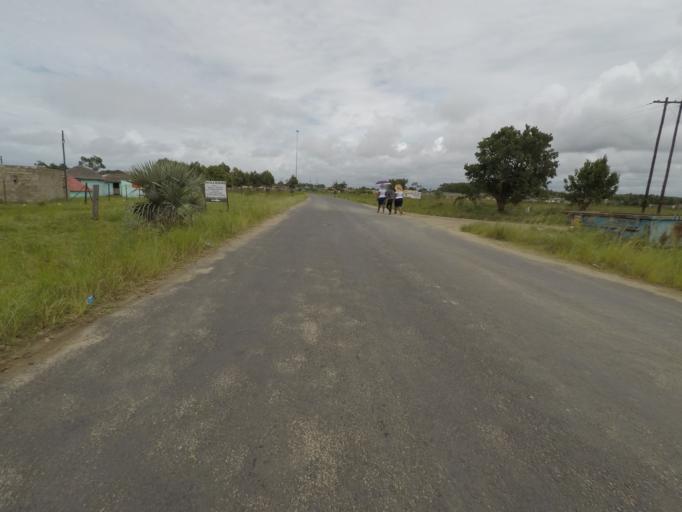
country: ZA
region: KwaZulu-Natal
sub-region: uThungulu District Municipality
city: eSikhawini
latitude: -28.9107
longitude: 31.8666
